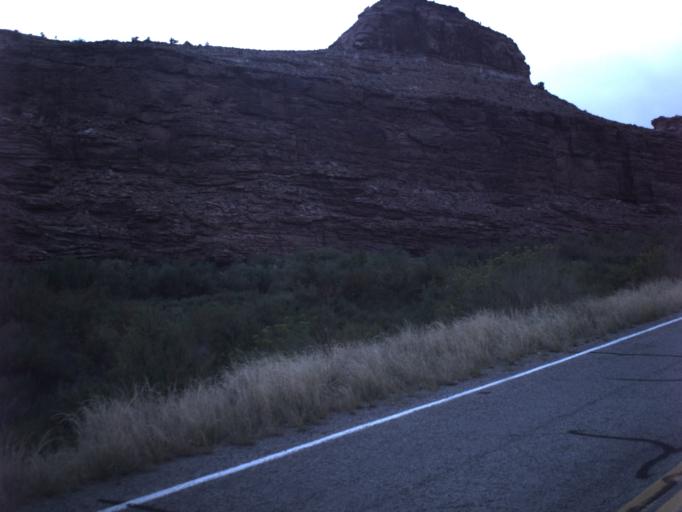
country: US
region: Utah
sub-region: Grand County
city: Moab
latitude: 38.8068
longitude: -109.3138
